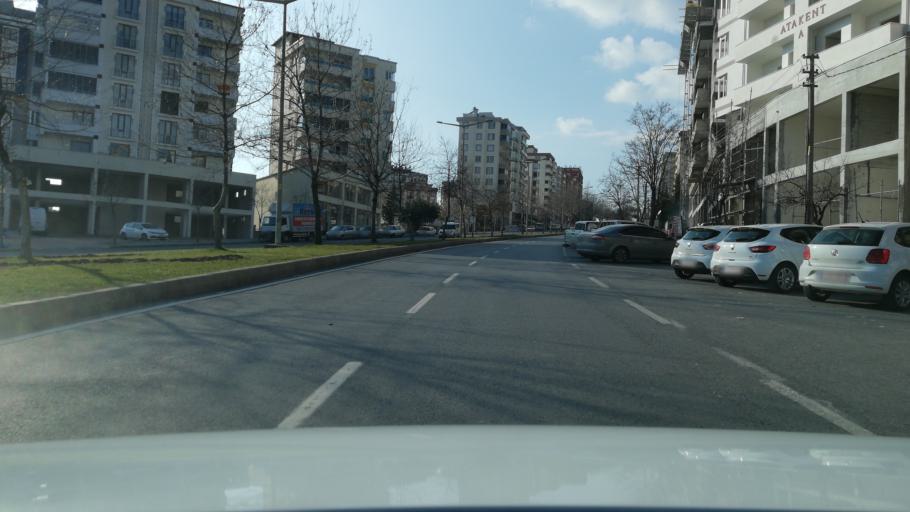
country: TR
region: Kahramanmaras
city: Kahramanmaras
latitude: 37.5928
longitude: 36.8985
